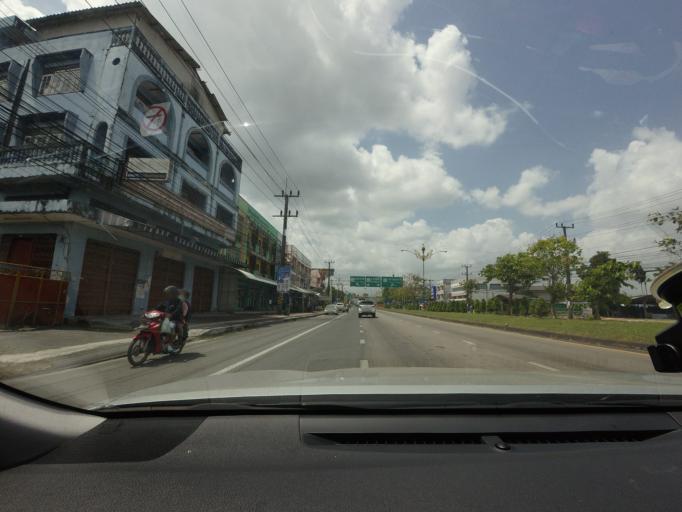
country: TH
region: Nakhon Si Thammarat
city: Nakhon Si Thammarat
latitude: 8.4340
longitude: 99.9243
